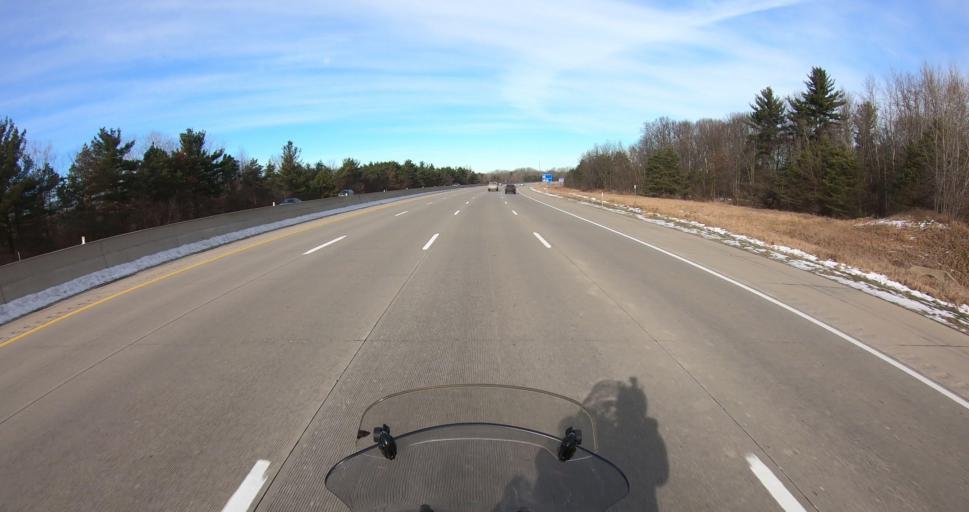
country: US
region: Michigan
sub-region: Saginaw County
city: Bridgeport
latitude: 43.3333
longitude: -83.8595
